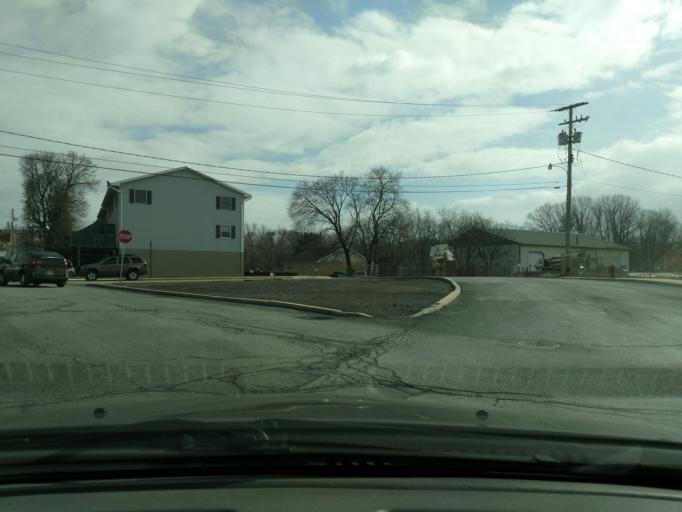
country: US
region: Pennsylvania
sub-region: Schuylkill County
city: Schuylkill Haven
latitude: 40.6354
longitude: -76.1763
